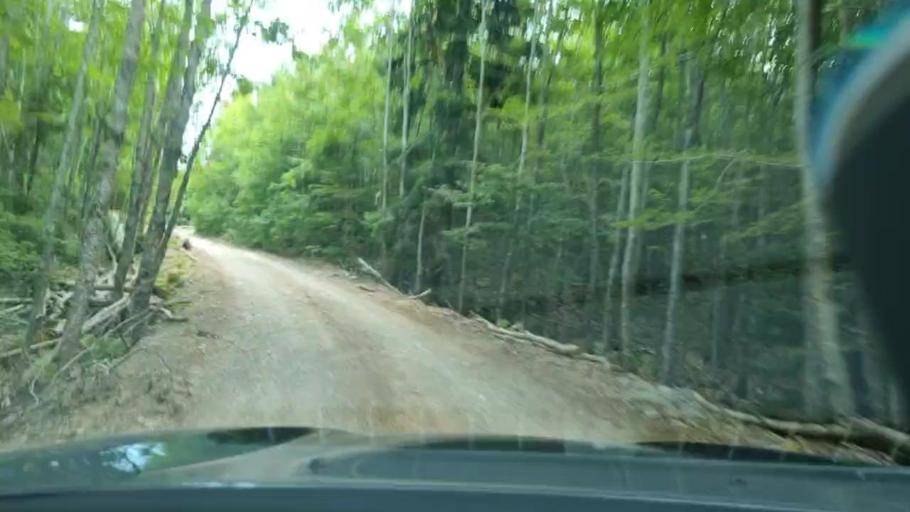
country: BA
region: Federation of Bosnia and Herzegovina
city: Bosansko Grahovo
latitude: 44.3218
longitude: 16.2437
